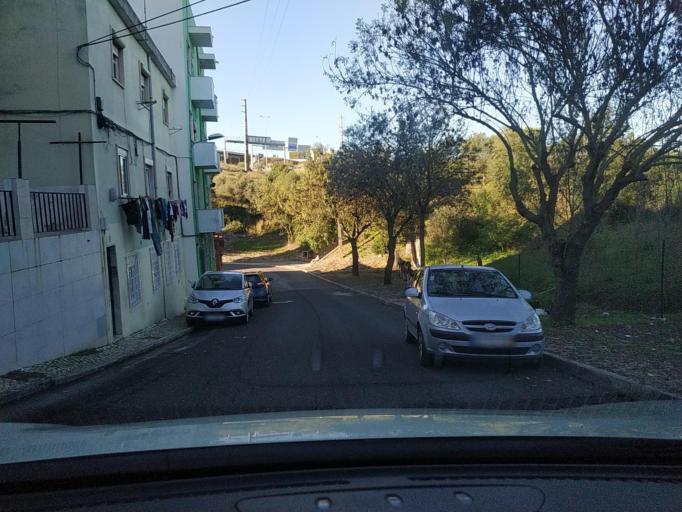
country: PT
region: Lisbon
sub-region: Odivelas
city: Pontinha
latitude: 38.7711
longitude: -9.2132
